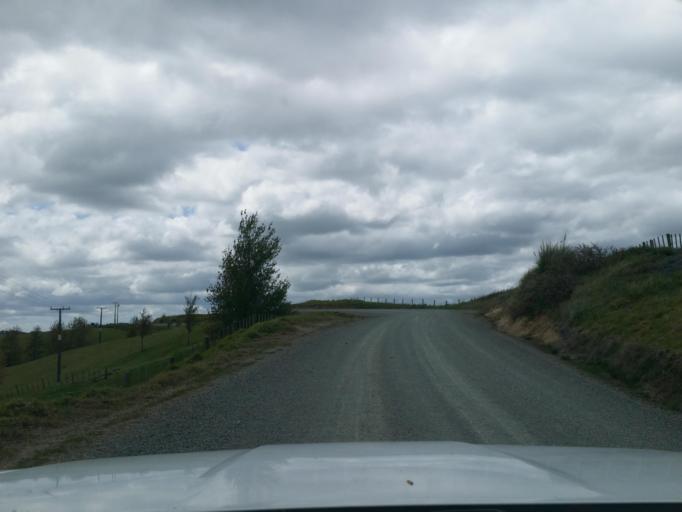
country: NZ
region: Auckland
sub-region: Auckland
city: Wellsford
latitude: -36.2791
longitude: 174.3644
